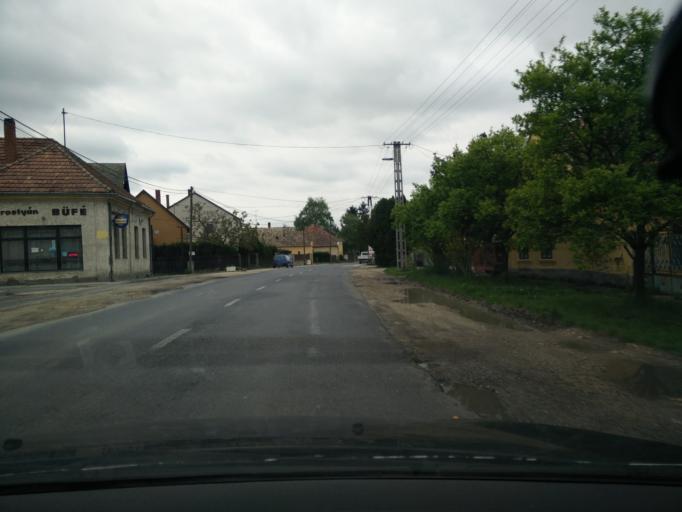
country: HU
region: Veszprem
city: Papa
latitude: 47.3962
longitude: 17.4737
